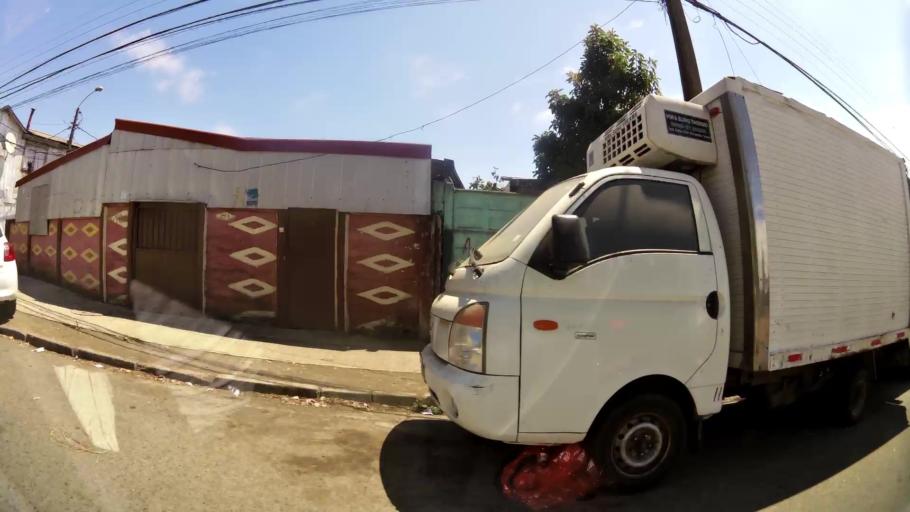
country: CL
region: Biobio
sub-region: Provincia de Concepcion
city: Concepcion
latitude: -36.8019
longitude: -73.0539
